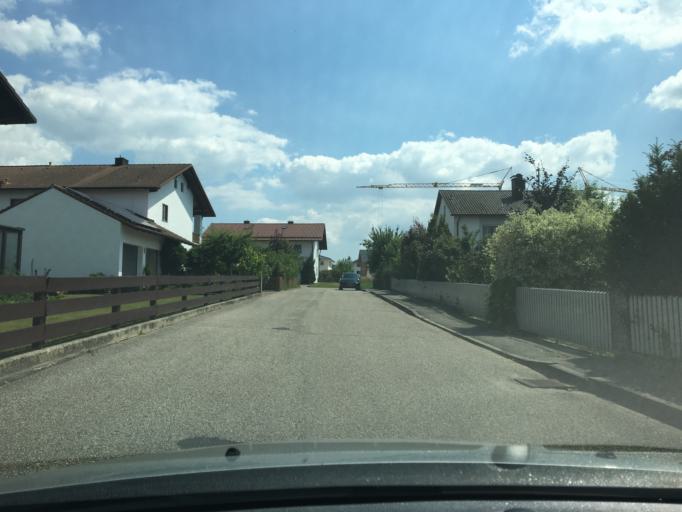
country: DE
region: Bavaria
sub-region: Upper Bavaria
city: Neumarkt-Sankt Veit
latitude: 48.3559
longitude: 12.5081
